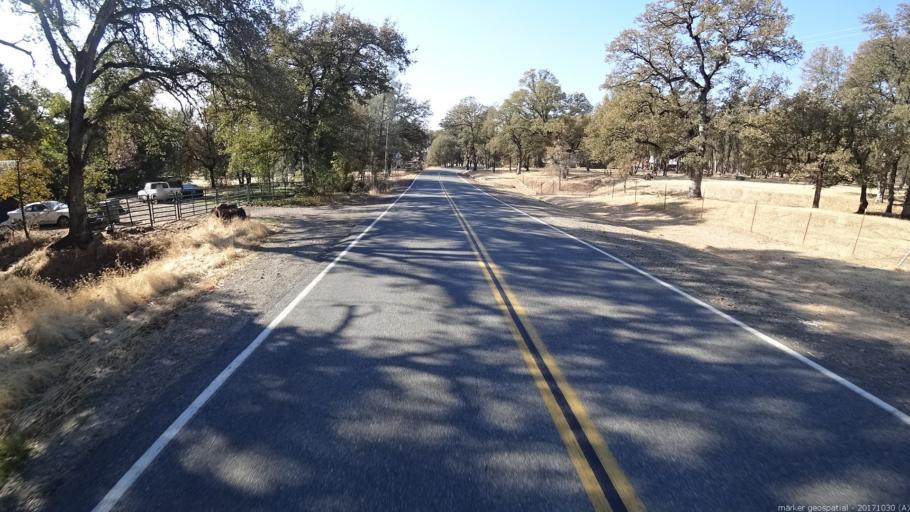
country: US
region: California
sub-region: Shasta County
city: Palo Cedro
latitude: 40.5715
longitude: -122.1901
